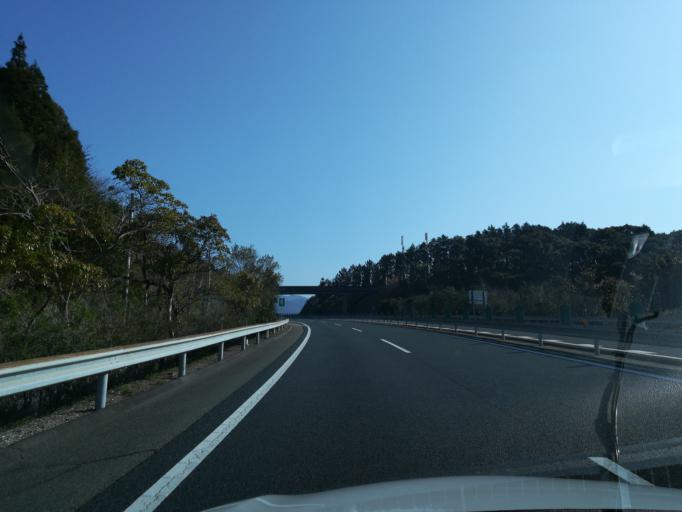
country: JP
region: Kochi
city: Kochi-shi
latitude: 33.6396
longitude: 133.6691
